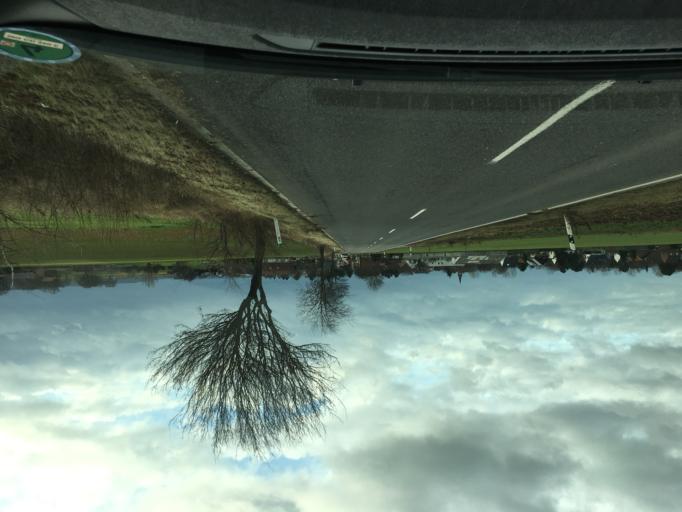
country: DE
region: North Rhine-Westphalia
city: Zulpich
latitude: 50.6725
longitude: 6.7079
